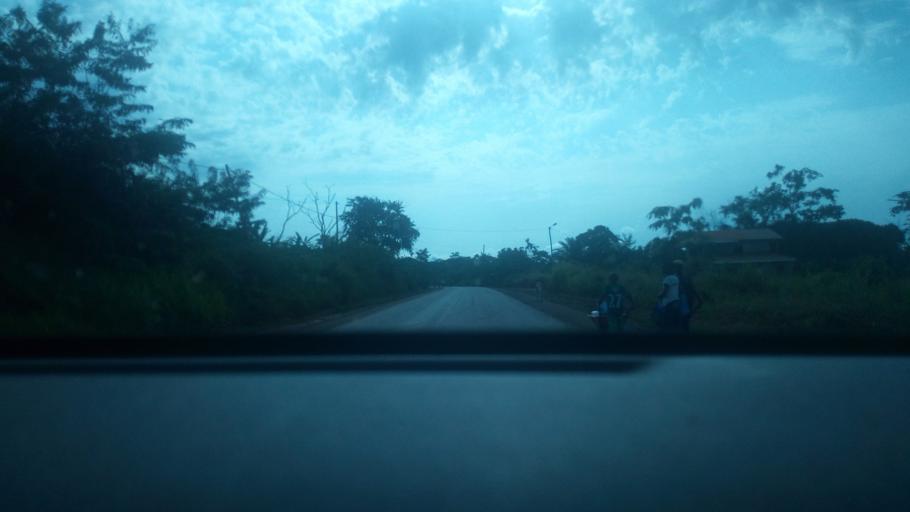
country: CM
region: Centre
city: Nkoteng
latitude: 4.5058
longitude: 12.1097
